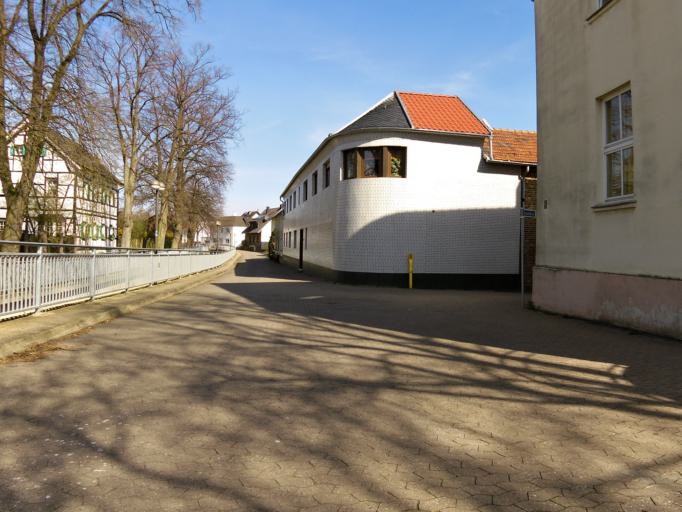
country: DE
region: North Rhine-Westphalia
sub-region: Regierungsbezirk Koln
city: Rheinbach
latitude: 50.6486
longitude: 6.9854
